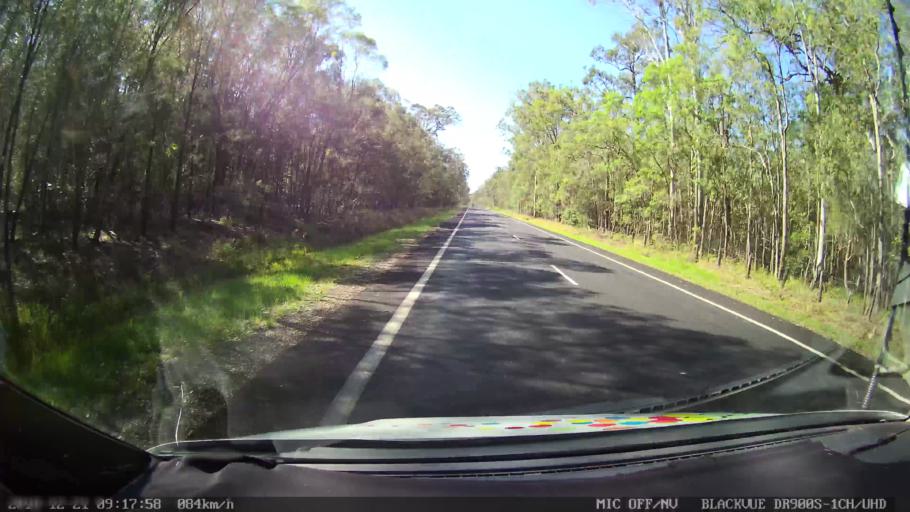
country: AU
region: New South Wales
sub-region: Clarence Valley
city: Maclean
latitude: -29.2986
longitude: 152.9924
